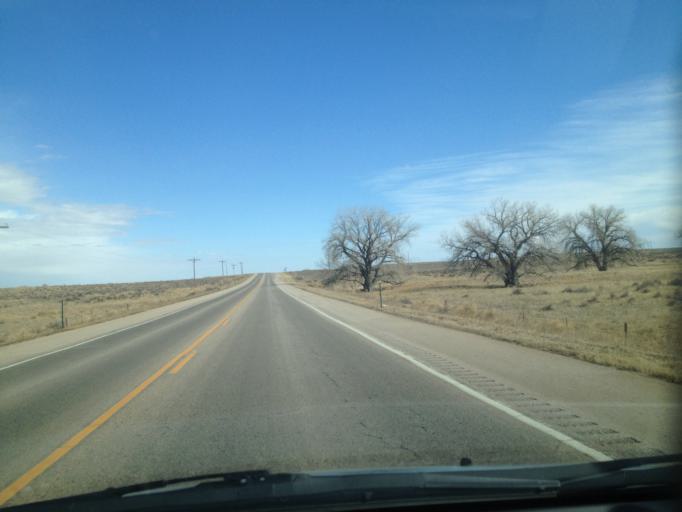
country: US
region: Colorado
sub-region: Weld County
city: Kersey
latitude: 40.2937
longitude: -104.2972
